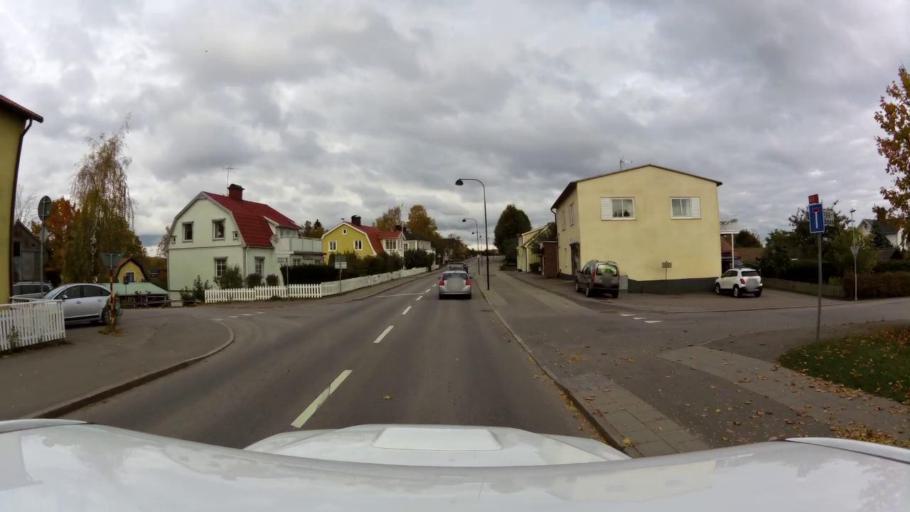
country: SE
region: OEstergoetland
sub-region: Linkopings Kommun
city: Berg
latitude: 58.4864
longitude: 15.5253
